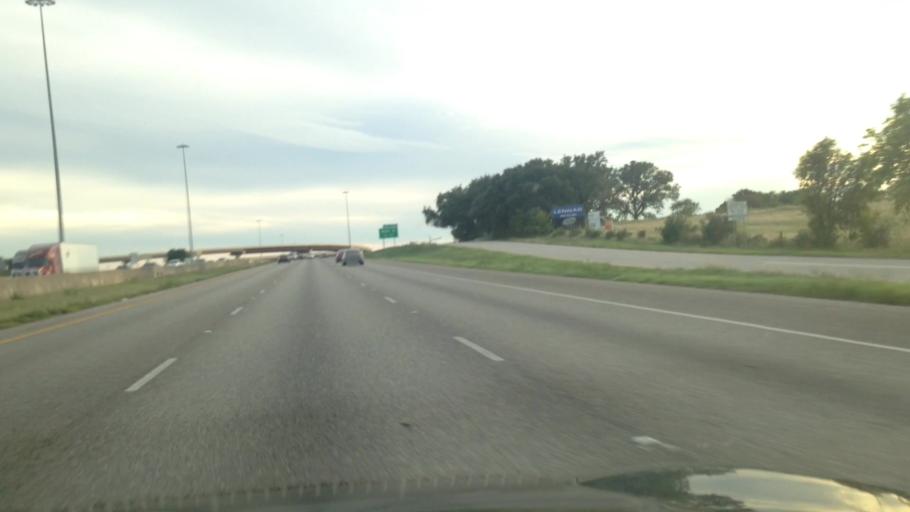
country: US
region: Texas
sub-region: Travis County
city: Onion Creek
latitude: 30.1174
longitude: -97.8052
